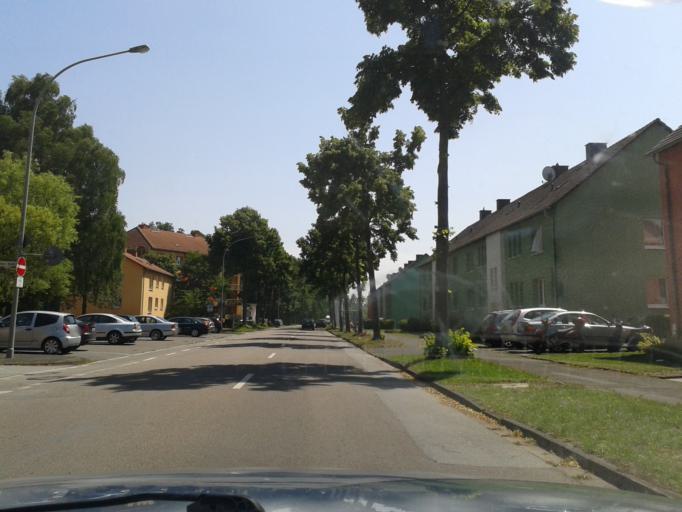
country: DE
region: North Rhine-Westphalia
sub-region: Regierungsbezirk Detmold
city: Paderborn
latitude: 51.7512
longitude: 8.7642
